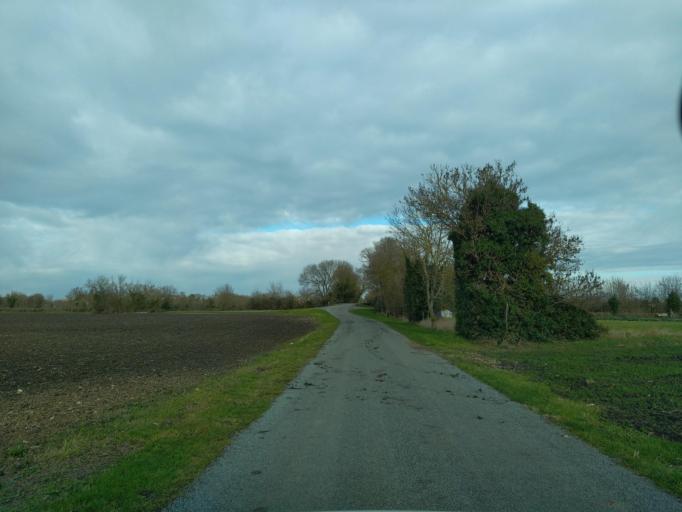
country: FR
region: Pays de la Loire
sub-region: Departement de la Vendee
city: Maillezais
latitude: 46.3362
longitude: -0.7894
